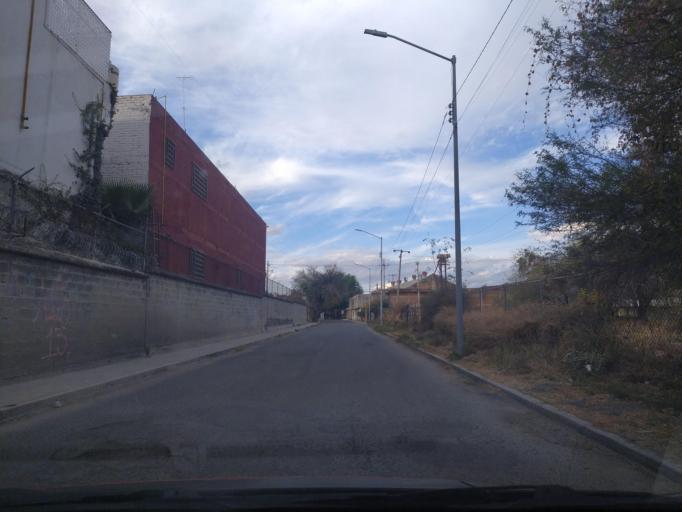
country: LA
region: Oudomxai
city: Muang La
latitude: 21.0327
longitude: 101.8836
